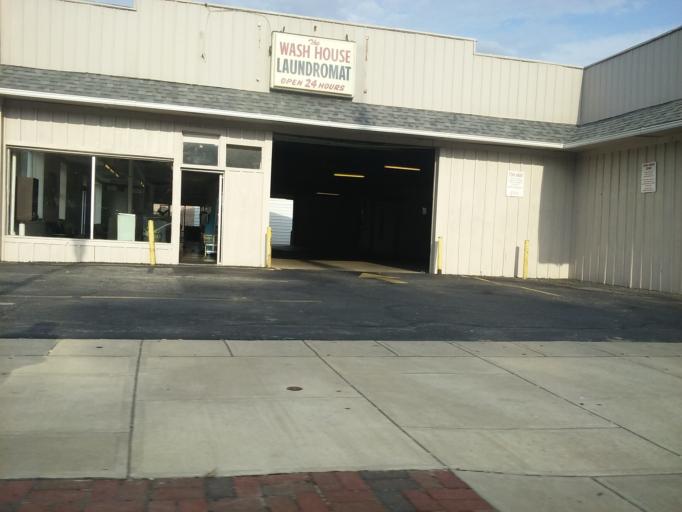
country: US
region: Ohio
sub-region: Wood County
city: Bowling Green
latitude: 41.3767
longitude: -83.6503
